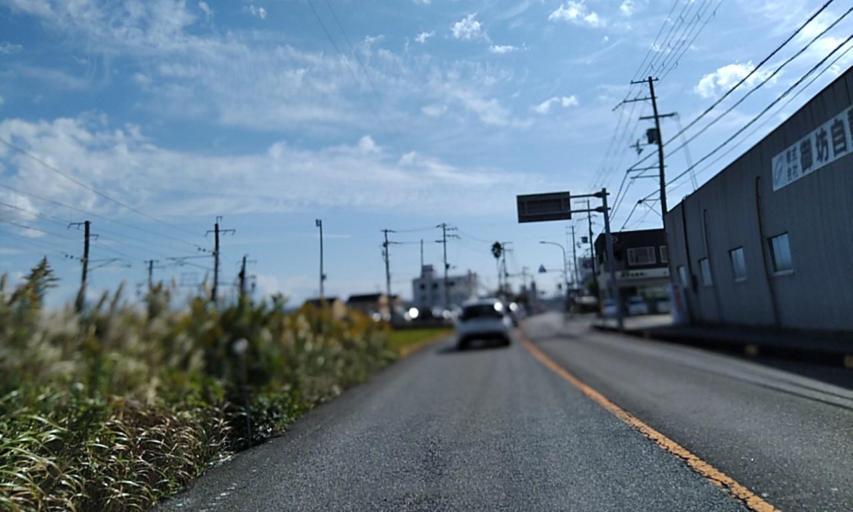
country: JP
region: Wakayama
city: Gobo
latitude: 33.9087
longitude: 135.1506
